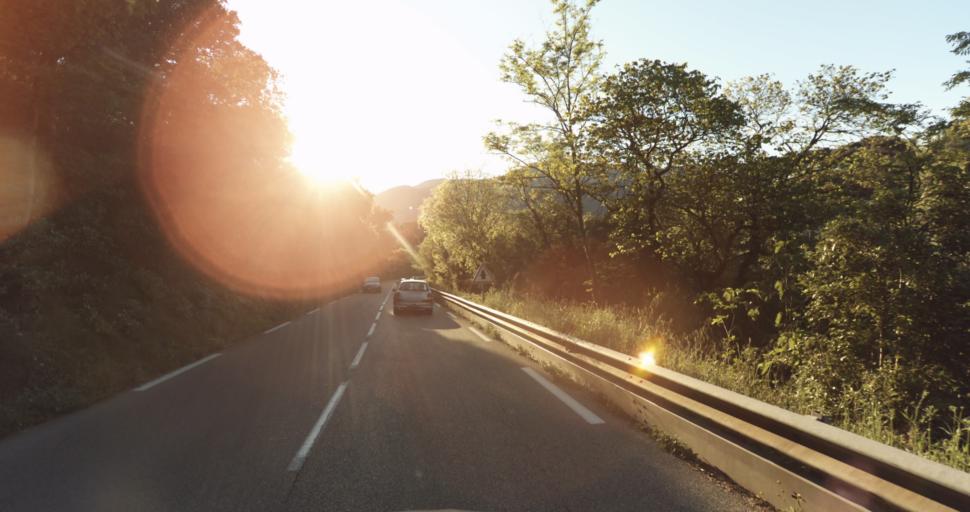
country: FR
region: Provence-Alpes-Cote d'Azur
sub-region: Departement du Var
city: Le Revest-les-Eaux
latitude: 43.1644
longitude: 5.9415
